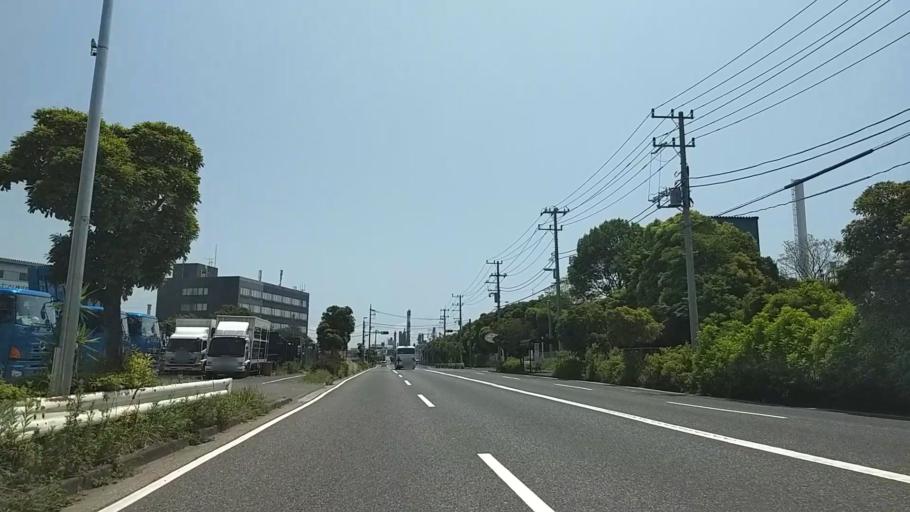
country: JP
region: Kanagawa
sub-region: Kawasaki-shi
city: Kawasaki
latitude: 35.5198
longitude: 139.7335
